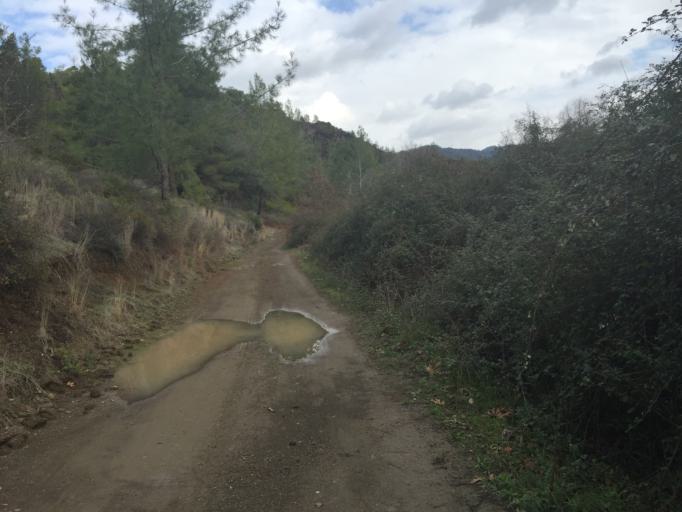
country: CY
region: Limassol
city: Pachna
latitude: 34.8874
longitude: 32.6782
